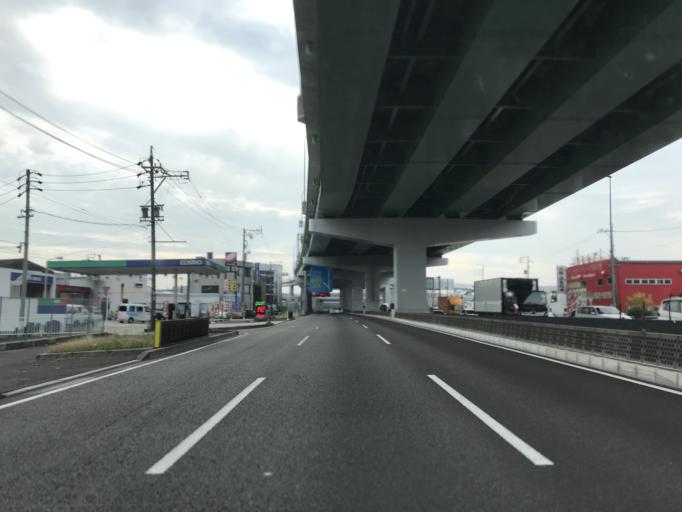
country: JP
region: Aichi
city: Iwakura
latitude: 35.2264
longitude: 136.8532
